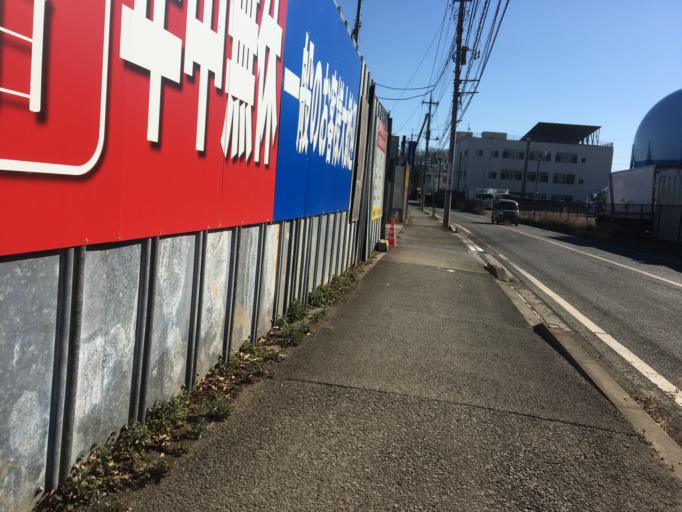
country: JP
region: Saitama
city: Oi
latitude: 35.8294
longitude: 139.5246
